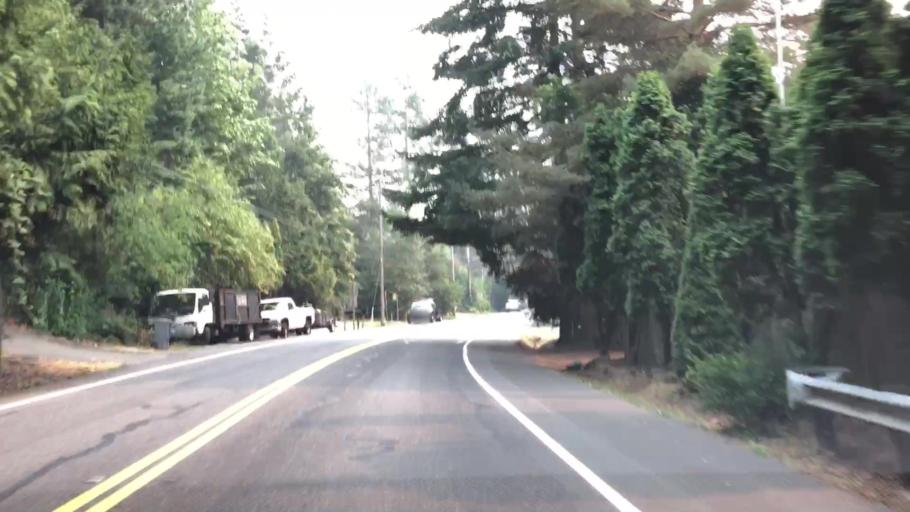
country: US
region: Washington
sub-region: King County
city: Lake Forest Park
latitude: 47.7710
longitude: -122.2923
